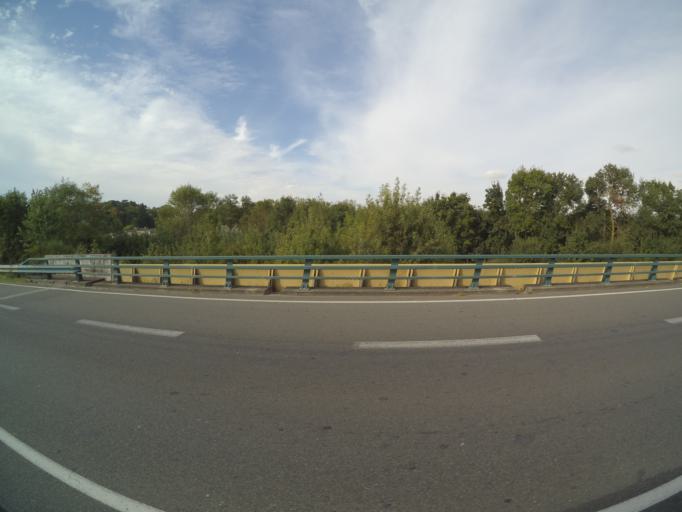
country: FR
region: Pays de la Loire
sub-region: Departement de Maine-et-Loire
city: Saumur
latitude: 47.2625
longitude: -0.0957
